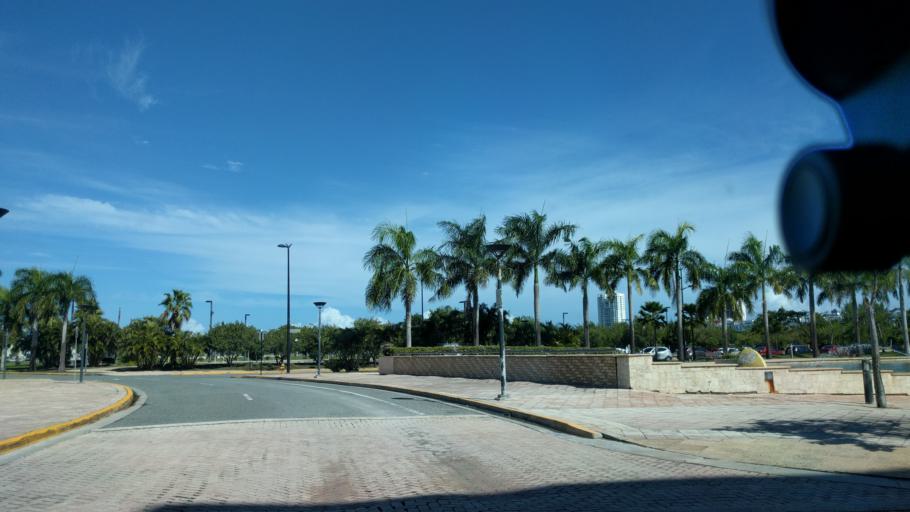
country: PR
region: San Juan
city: San Juan
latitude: 18.4546
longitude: -66.0910
